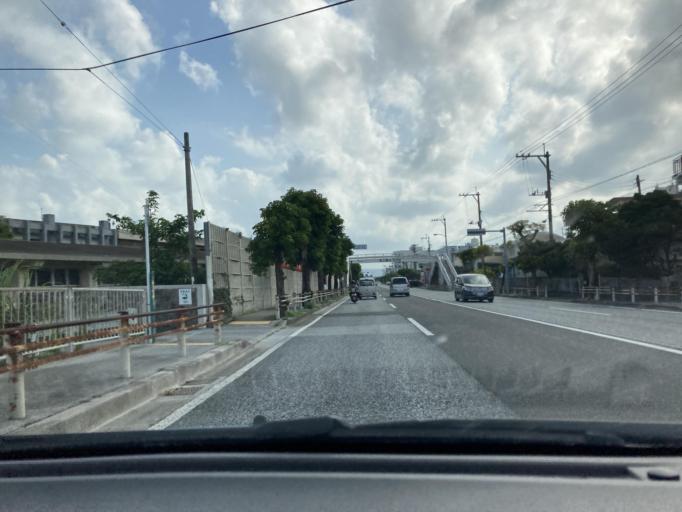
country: JP
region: Okinawa
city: Ginowan
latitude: 26.2692
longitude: 127.7913
